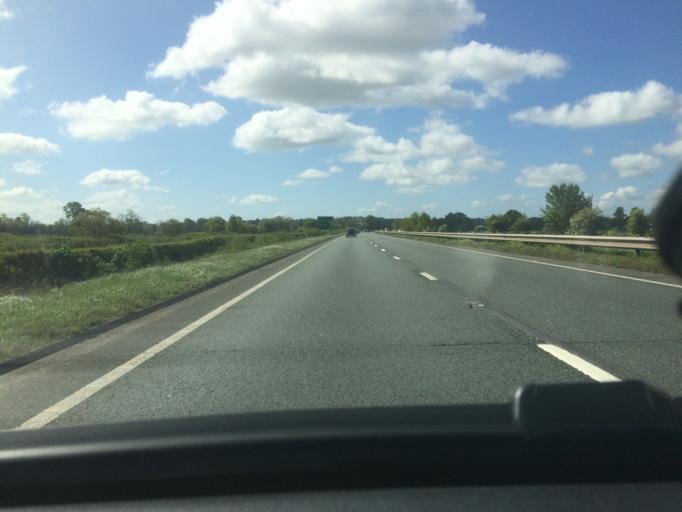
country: GB
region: Wales
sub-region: Wrexham
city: Rossett
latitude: 53.1178
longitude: -2.9510
